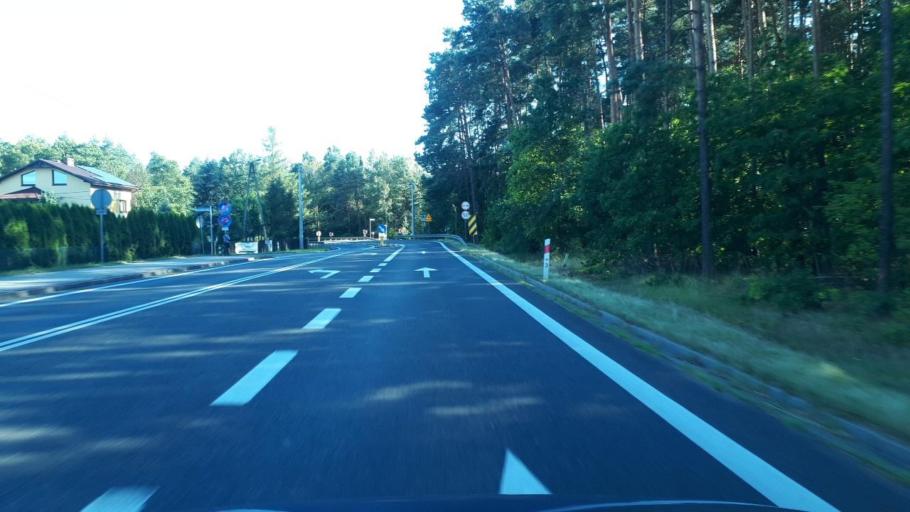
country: PL
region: Silesian Voivodeship
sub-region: Powiat tarnogorski
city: Tworog
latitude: 50.5925
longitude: 18.7009
